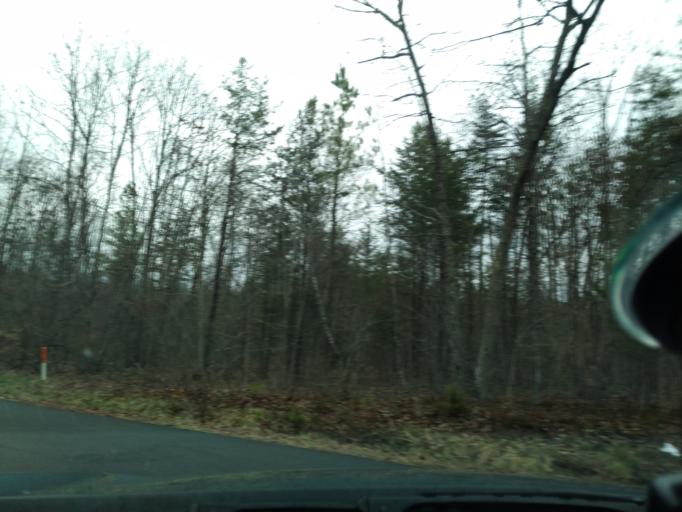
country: US
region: Virginia
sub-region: Appomattox County
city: Appomattox
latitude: 37.4125
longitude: -78.6760
